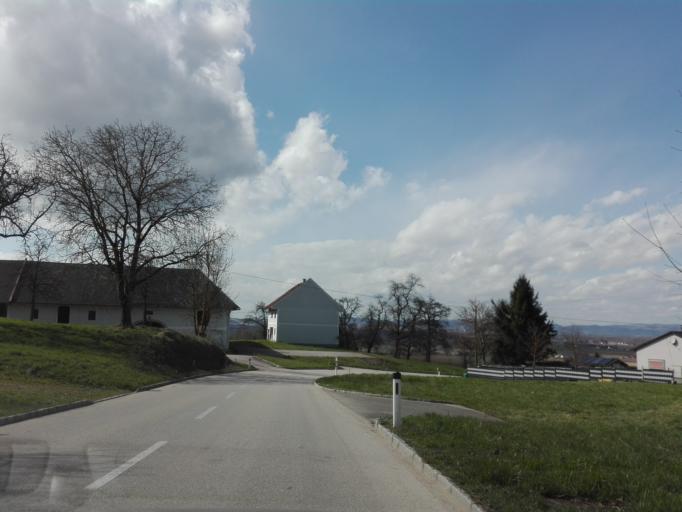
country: AT
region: Upper Austria
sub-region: Wels-Land
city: Holzhausen
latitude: 48.2664
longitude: 14.1165
